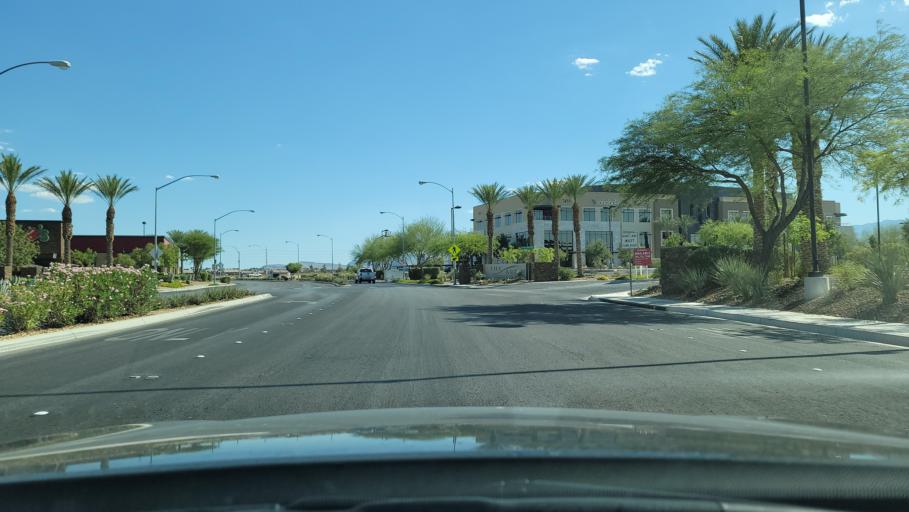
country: US
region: Nevada
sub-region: Clark County
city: Enterprise
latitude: 36.0638
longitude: -115.2524
